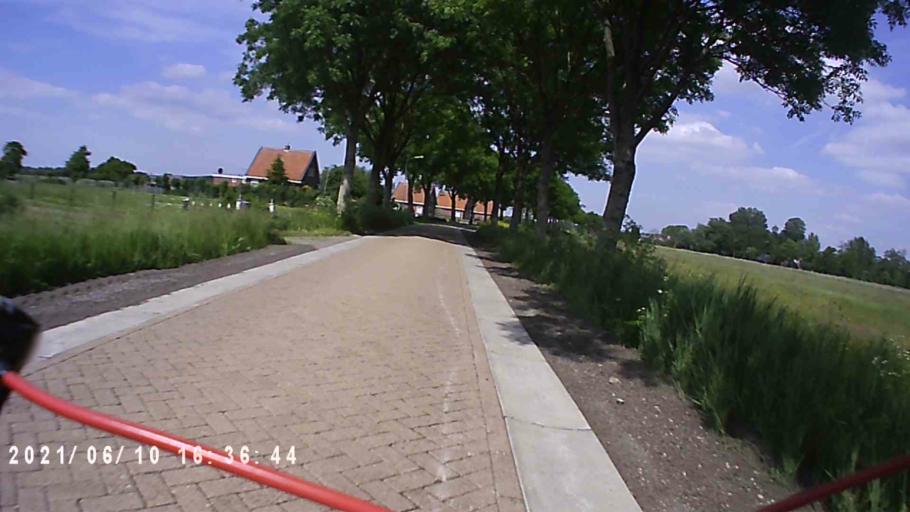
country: NL
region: Friesland
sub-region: Gemeente Achtkarspelen
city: Buitenpost
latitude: 53.2383
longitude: 6.1400
